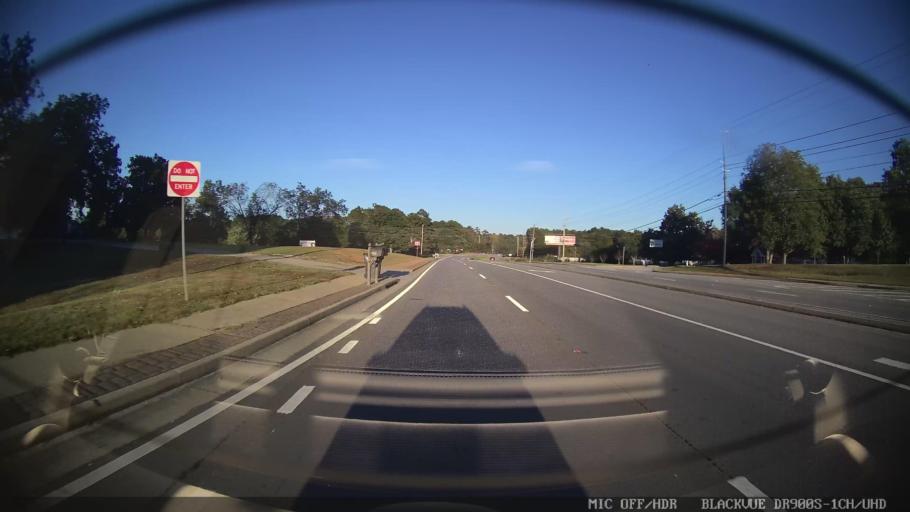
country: US
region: Georgia
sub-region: Clayton County
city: Jonesboro
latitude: 33.5402
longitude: -84.2993
